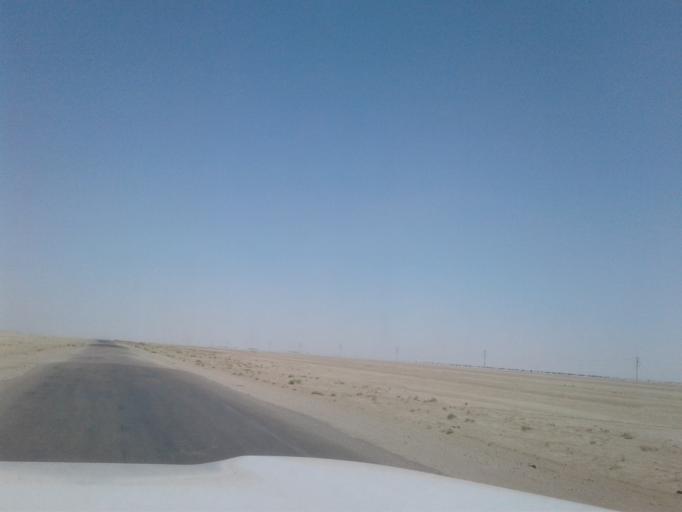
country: TM
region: Balkan
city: Gumdag
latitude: 38.7468
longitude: 54.5355
